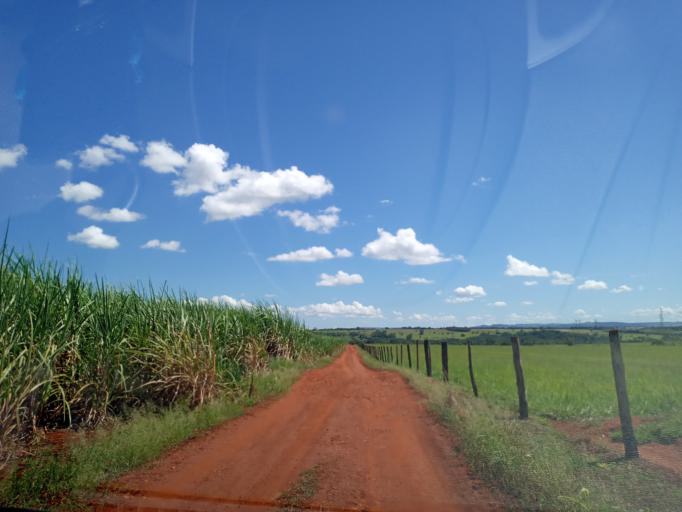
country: BR
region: Goias
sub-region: Itumbiara
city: Itumbiara
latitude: -18.4029
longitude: -49.1299
